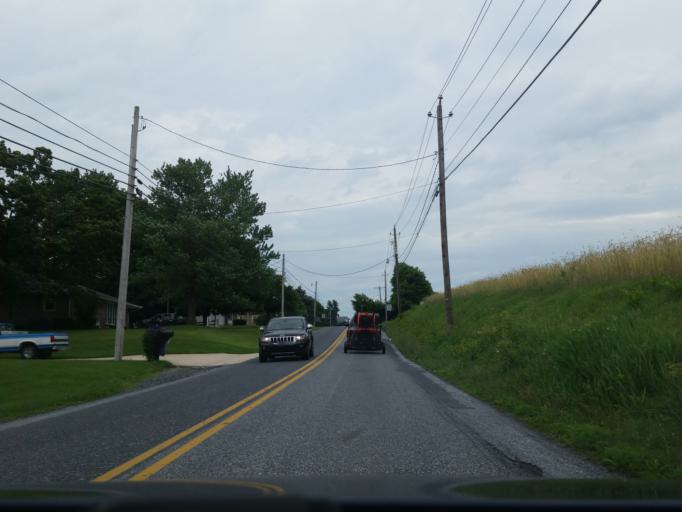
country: US
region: Pennsylvania
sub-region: Lebanon County
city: Jonestown
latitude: 40.4023
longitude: -76.5432
